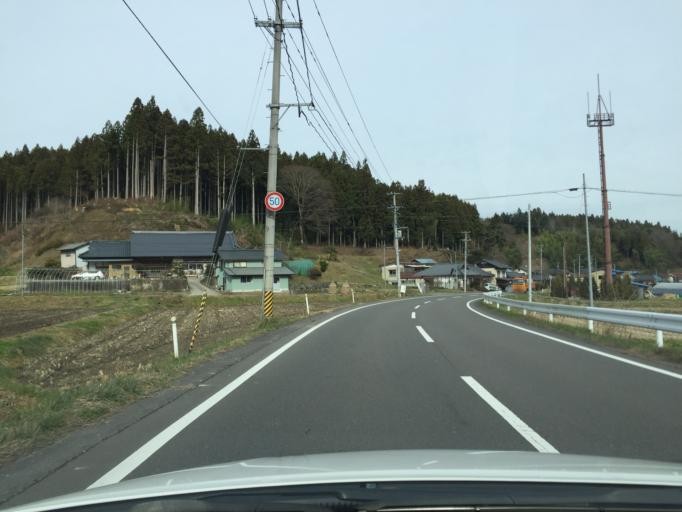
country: JP
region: Fukushima
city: Ishikawa
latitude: 37.2145
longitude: 140.6255
